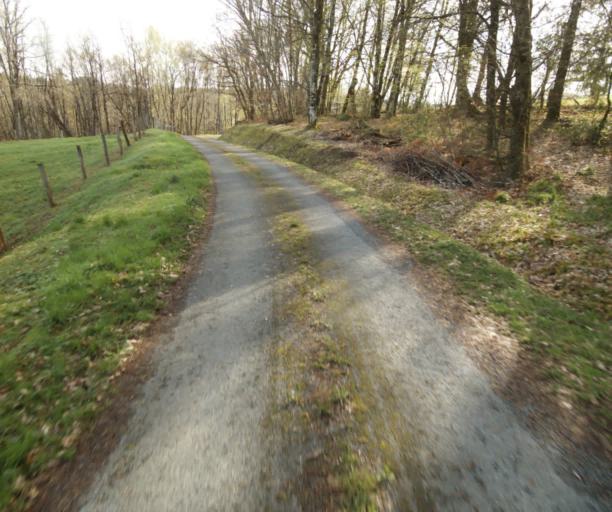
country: FR
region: Limousin
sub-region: Departement de la Correze
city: Naves
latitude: 45.3265
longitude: 1.8197
